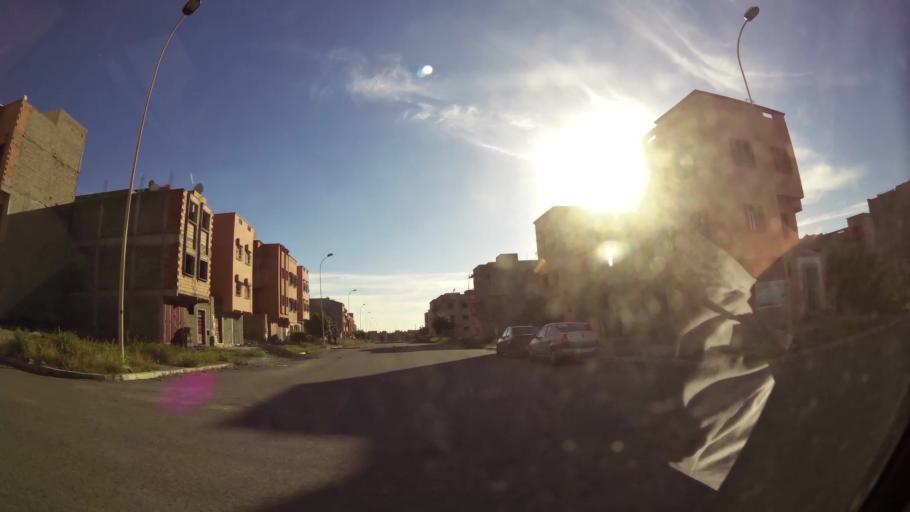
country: MA
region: Marrakech-Tensift-Al Haouz
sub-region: Marrakech
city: Marrakesh
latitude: 31.7592
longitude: -8.1006
